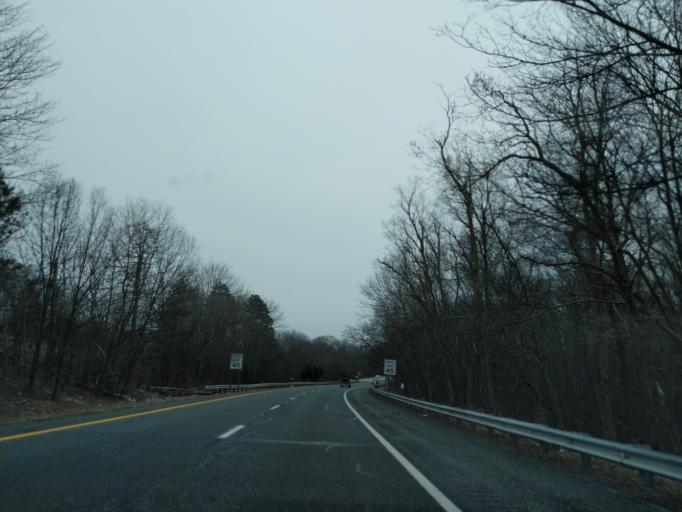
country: US
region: Rhode Island
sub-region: Providence County
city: Woonsocket
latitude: 41.9705
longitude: -71.5107
